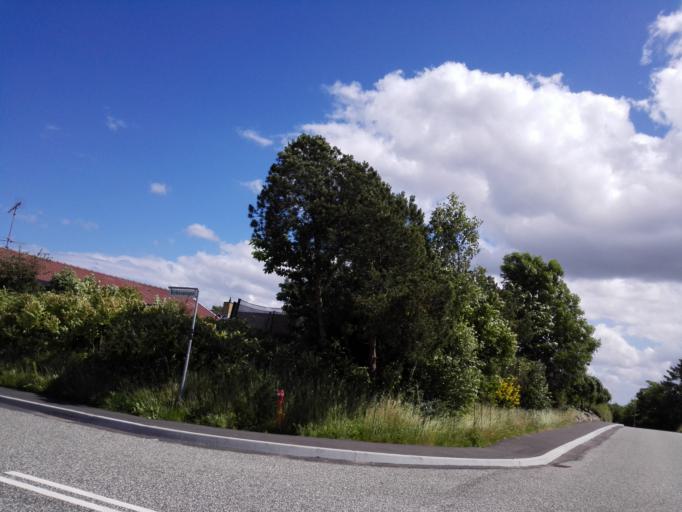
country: DK
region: Capital Region
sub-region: Allerod Kommune
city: Lynge
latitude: 55.8400
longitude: 12.2627
